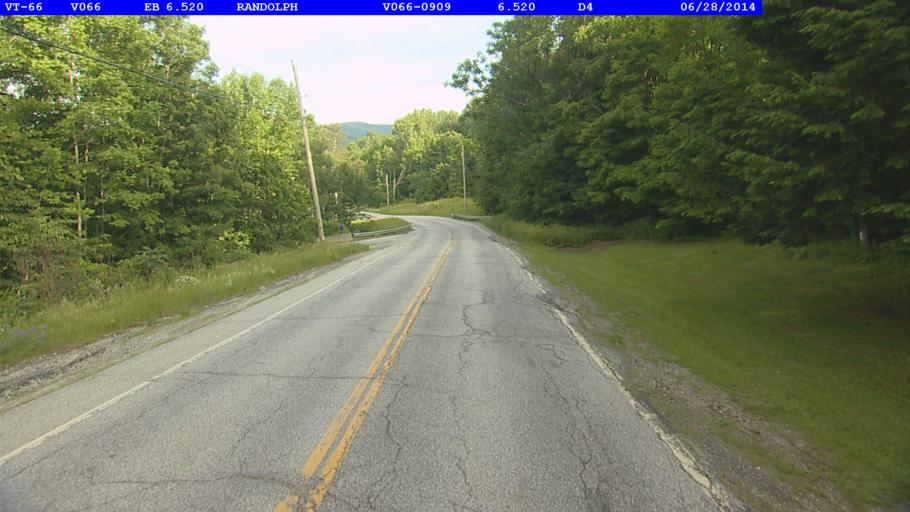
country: US
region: Vermont
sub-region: Orange County
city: Randolph
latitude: 43.9522
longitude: -72.5656
